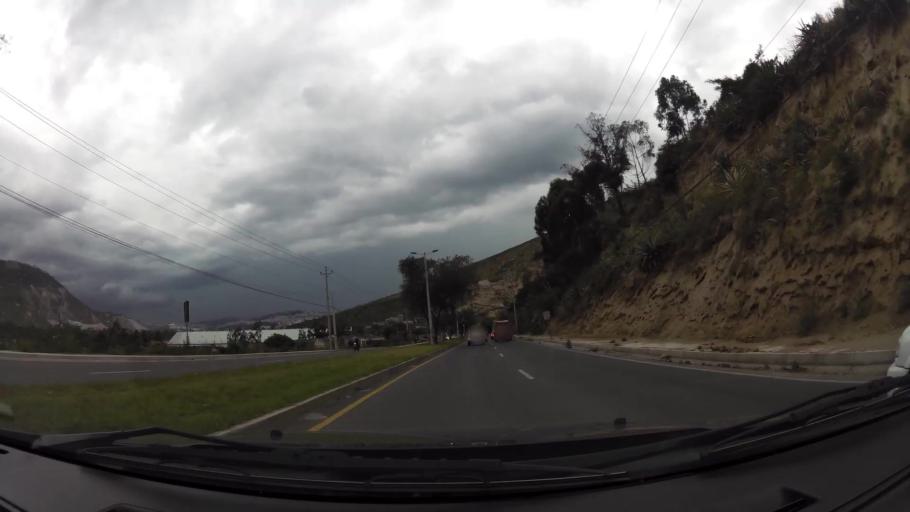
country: EC
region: Pichincha
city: Quito
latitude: -0.0297
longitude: -78.4523
